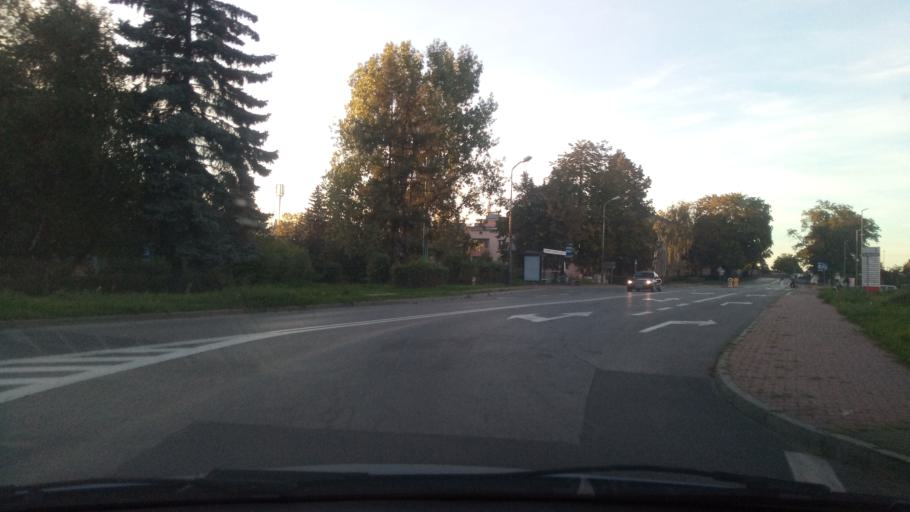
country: PL
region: Silesian Voivodeship
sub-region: Sosnowiec
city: Sosnowiec
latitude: 50.2894
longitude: 19.0815
